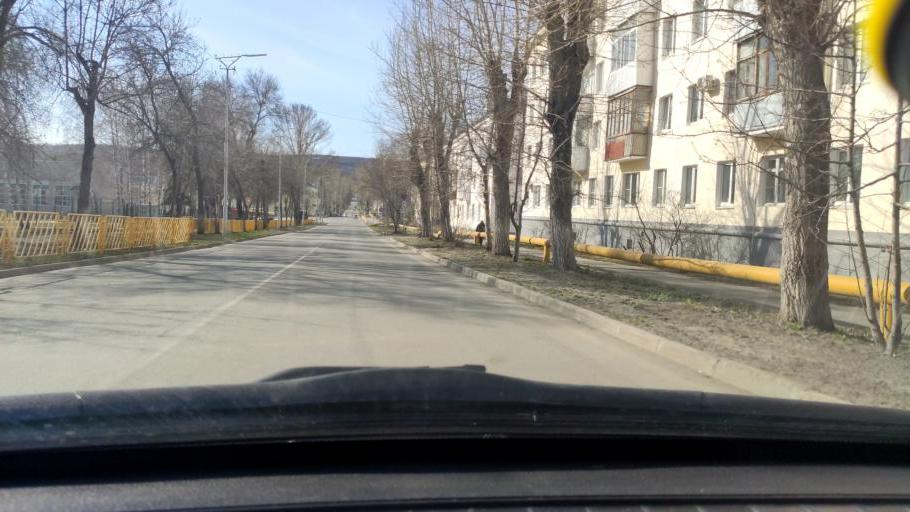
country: RU
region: Samara
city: Zhigulevsk
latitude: 53.4037
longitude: 49.4977
